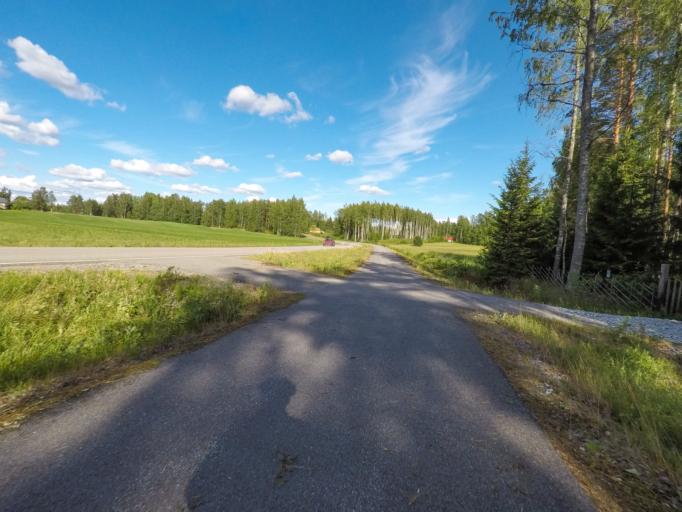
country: FI
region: South Karelia
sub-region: Lappeenranta
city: Joutseno
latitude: 61.1531
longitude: 28.5895
